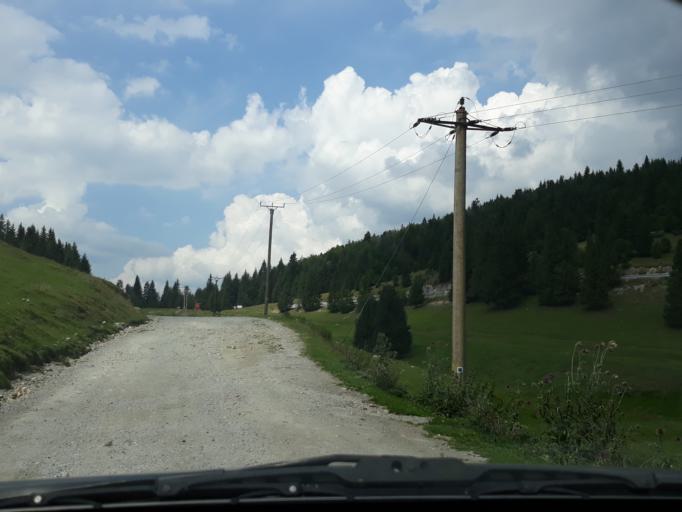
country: RO
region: Alba
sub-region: Comuna Arieseni
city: Arieseni
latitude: 46.5898
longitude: 22.6859
